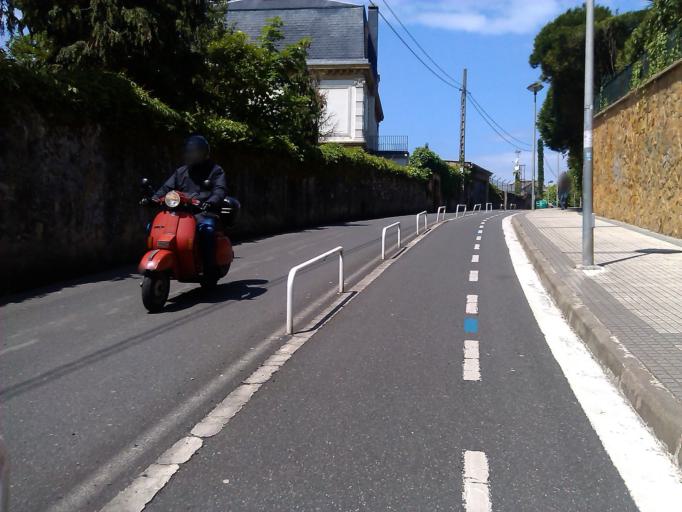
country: ES
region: Basque Country
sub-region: Provincia de Guipuzcoa
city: San Sebastian
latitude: 43.3224
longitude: -1.9625
